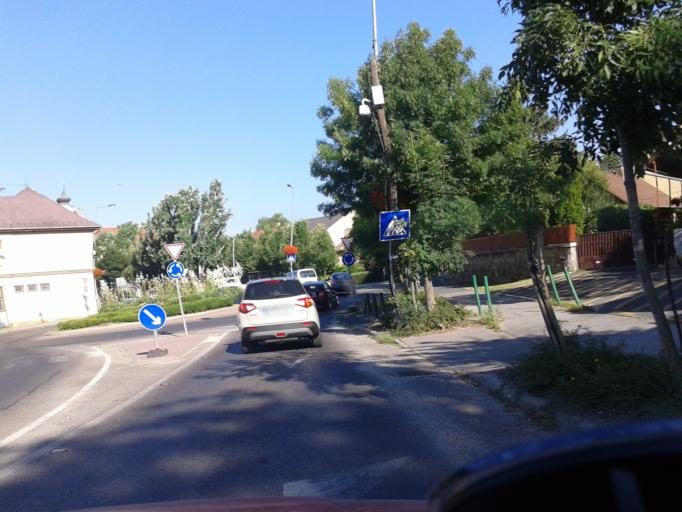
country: HU
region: Pest
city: Budaors
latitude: 47.4616
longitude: 18.9656
